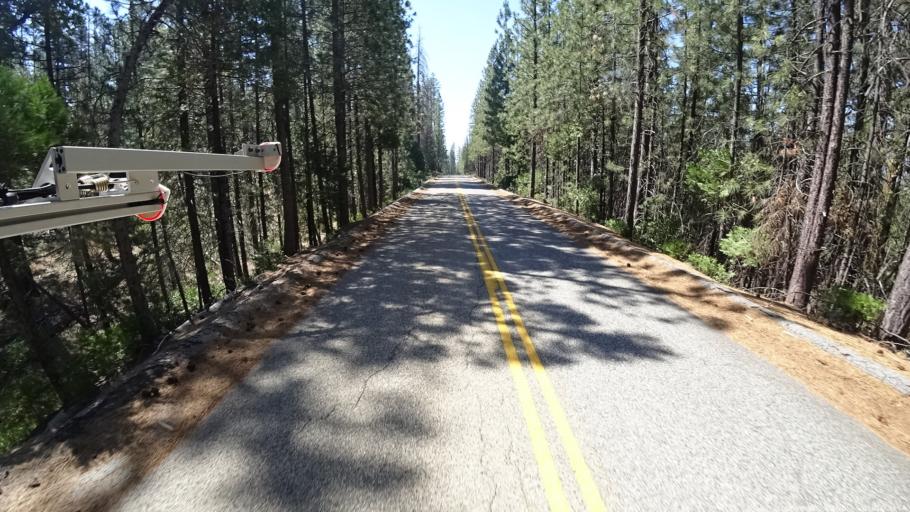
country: US
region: California
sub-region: Madera County
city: Oakhurst
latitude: 37.4055
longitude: -119.3479
